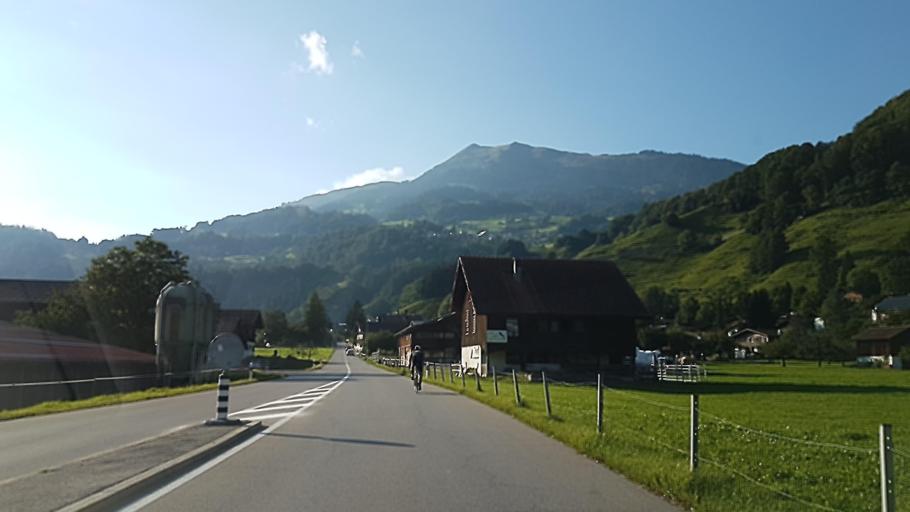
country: CH
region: Grisons
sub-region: Praettigau/Davos District
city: Grusch
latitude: 46.9783
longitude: 9.6562
